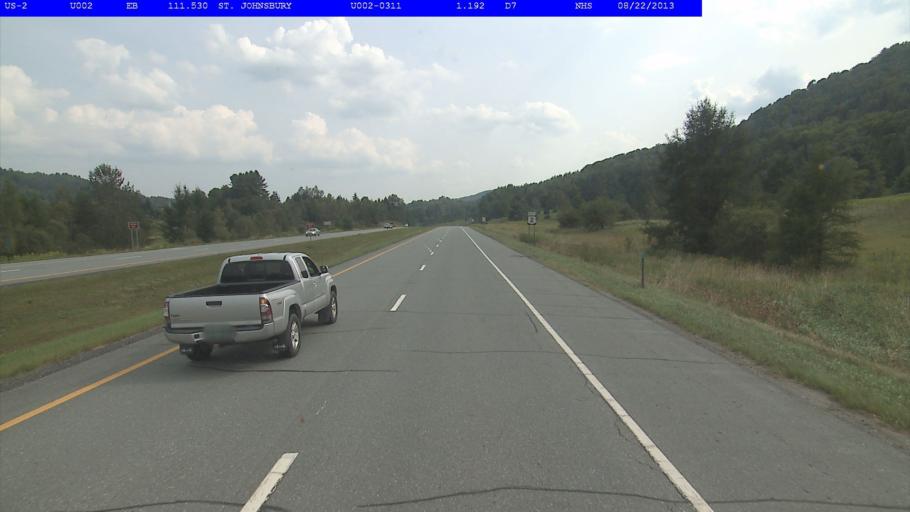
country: US
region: Vermont
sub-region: Caledonia County
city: St Johnsbury
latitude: 44.4375
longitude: -72.0422
